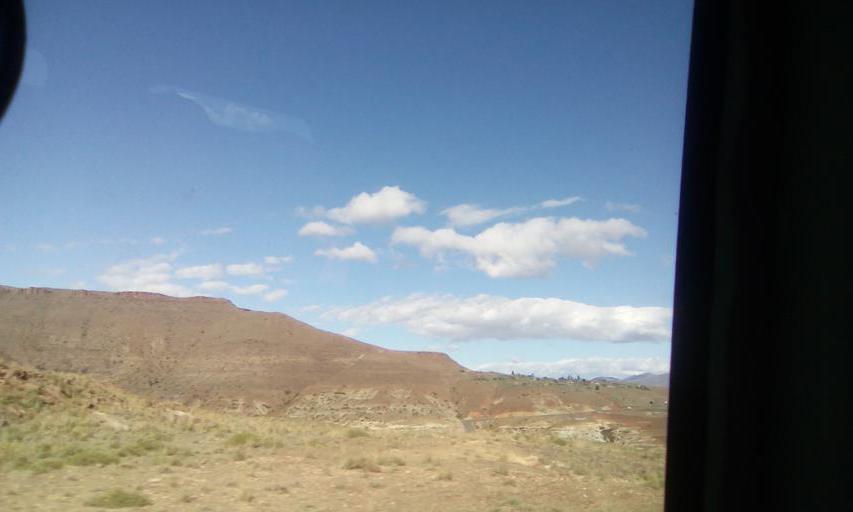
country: LS
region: Qacha's Nek
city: Qacha's Nek
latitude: -30.0554
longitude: 28.2962
